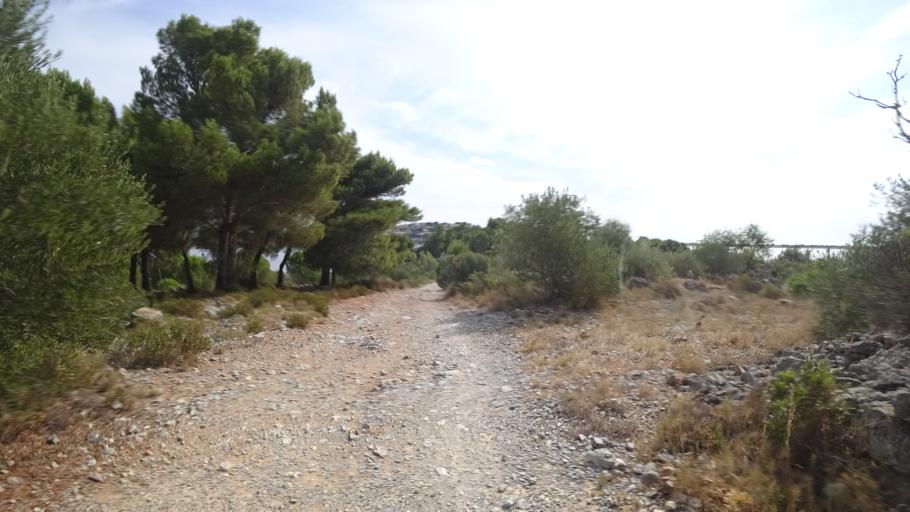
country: FR
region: Languedoc-Roussillon
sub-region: Departement de l'Aude
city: Leucate
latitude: 42.9004
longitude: 3.0389
